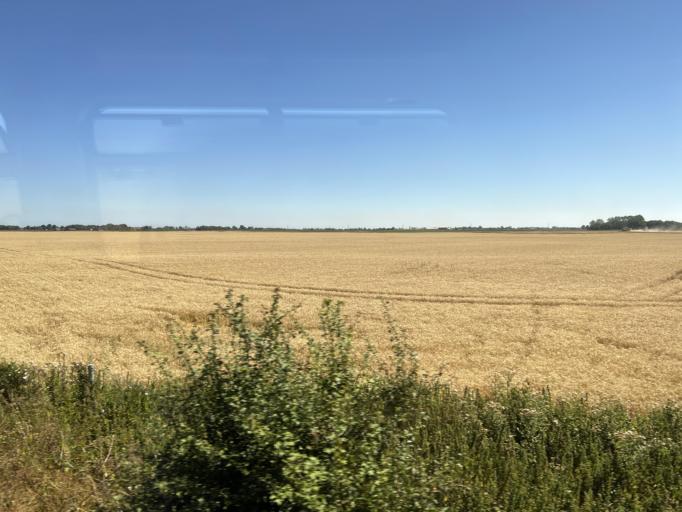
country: GB
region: England
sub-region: Lincolnshire
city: Spilsby
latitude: 53.0866
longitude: 0.0930
